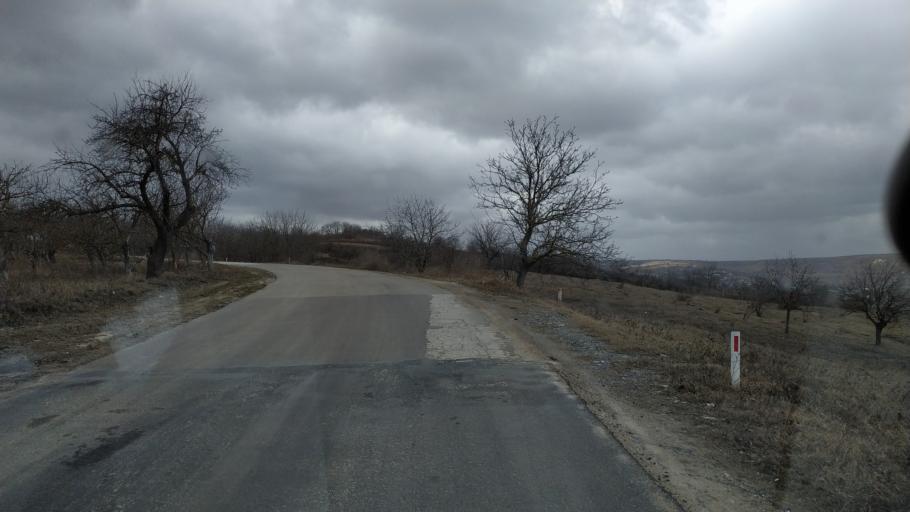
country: MD
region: Stinga Nistrului
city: Bucovat
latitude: 47.2217
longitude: 28.4235
